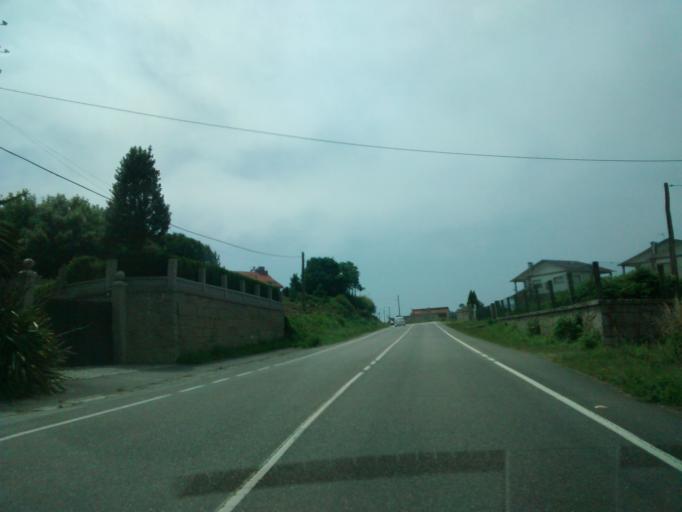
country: ES
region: Galicia
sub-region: Provincia de Pontevedra
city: Sanxenxo
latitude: 42.4078
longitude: -8.8540
